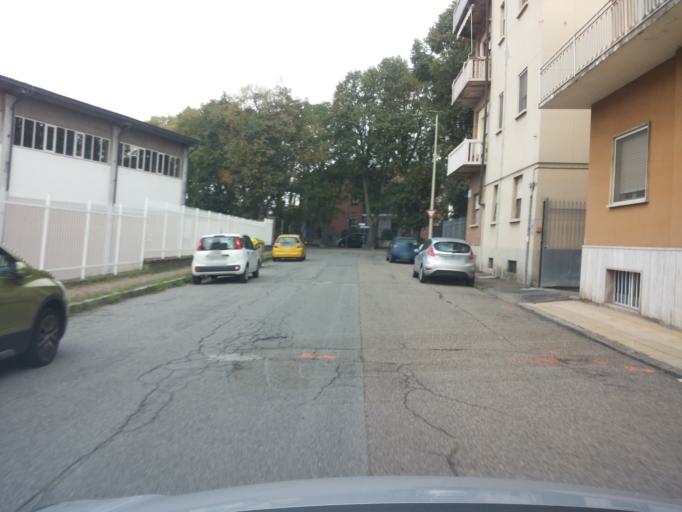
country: IT
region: Piedmont
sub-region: Provincia di Vercelli
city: Vercelli
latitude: 45.3315
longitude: 8.4245
